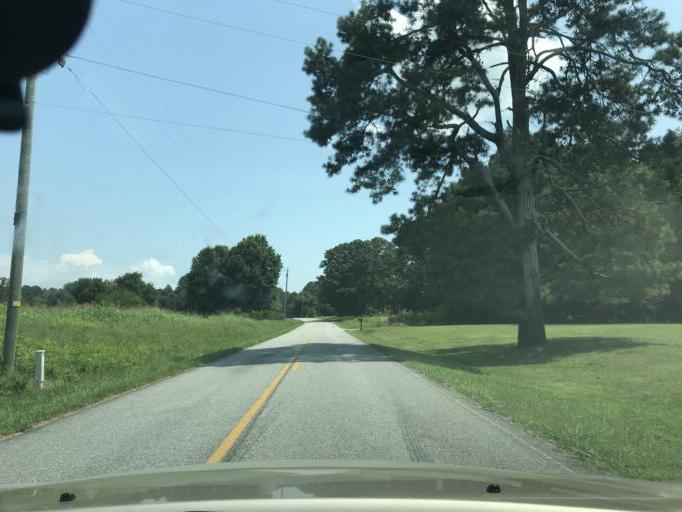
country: US
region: Georgia
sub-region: Dawson County
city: Dawsonville
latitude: 34.3230
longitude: -84.0919
